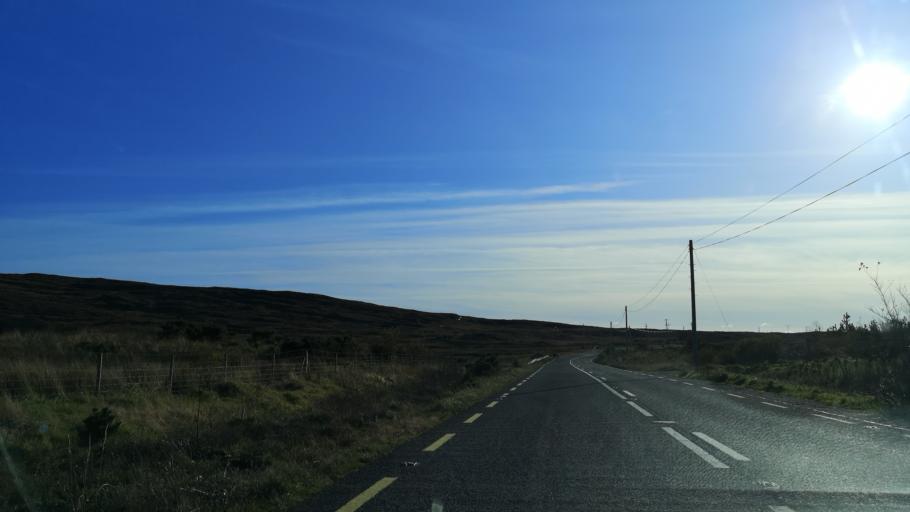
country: IE
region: Connaught
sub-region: County Galway
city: Clifden
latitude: 53.5334
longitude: -10.0382
